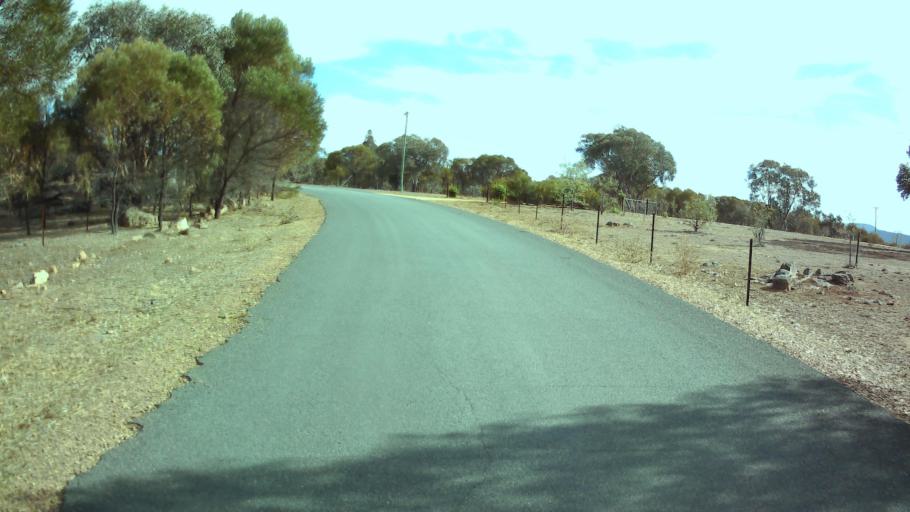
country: AU
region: New South Wales
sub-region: Weddin
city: Grenfell
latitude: -33.8760
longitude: 148.1925
